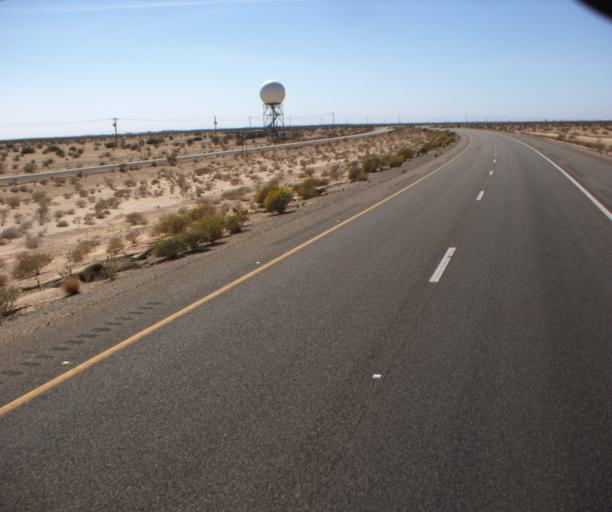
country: US
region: Arizona
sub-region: Yuma County
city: Somerton
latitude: 32.4966
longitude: -114.6541
